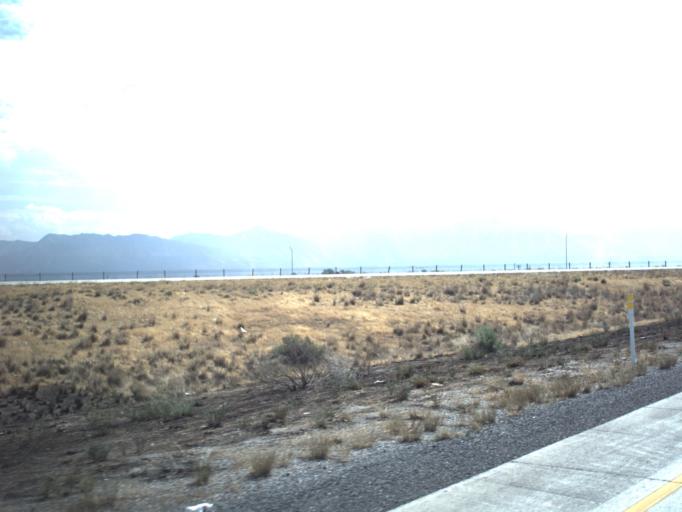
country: US
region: Utah
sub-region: Salt Lake County
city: West Valley City
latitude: 40.7623
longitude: -111.9880
